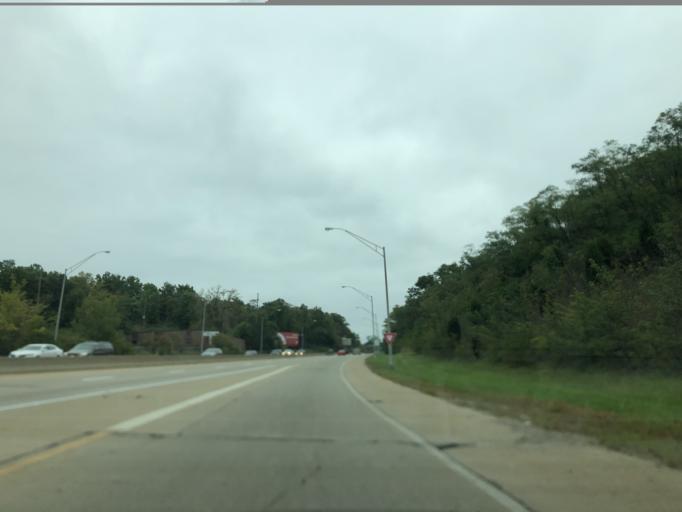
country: US
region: Ohio
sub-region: Hamilton County
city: Reading
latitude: 39.2127
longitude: -84.4393
